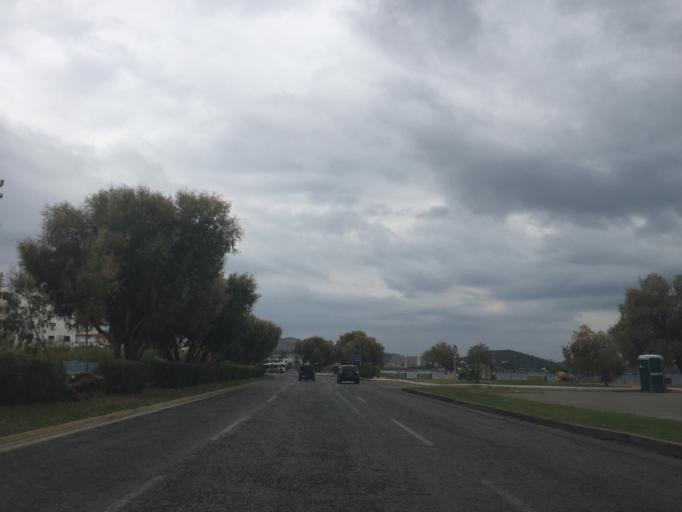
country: GR
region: Attica
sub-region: Nomarchia Anatolikis Attikis
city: Voula
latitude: 37.8386
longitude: 23.7627
